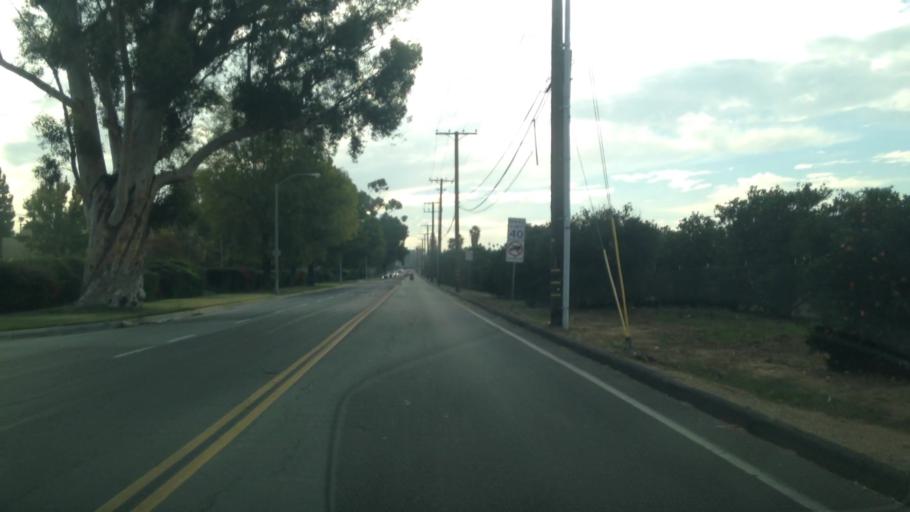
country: US
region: California
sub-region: Riverside County
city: Riverside
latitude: 33.9298
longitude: -117.3891
